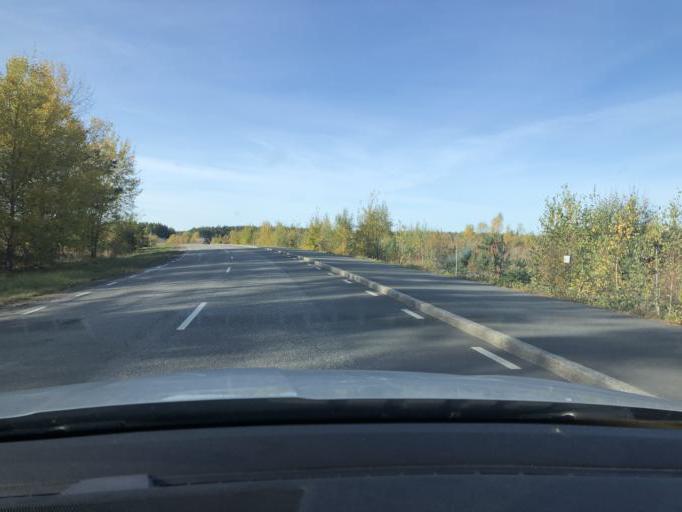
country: SE
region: Joenkoeping
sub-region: Jonkopings Kommun
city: Jonkoping
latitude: 57.7731
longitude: 14.0851
